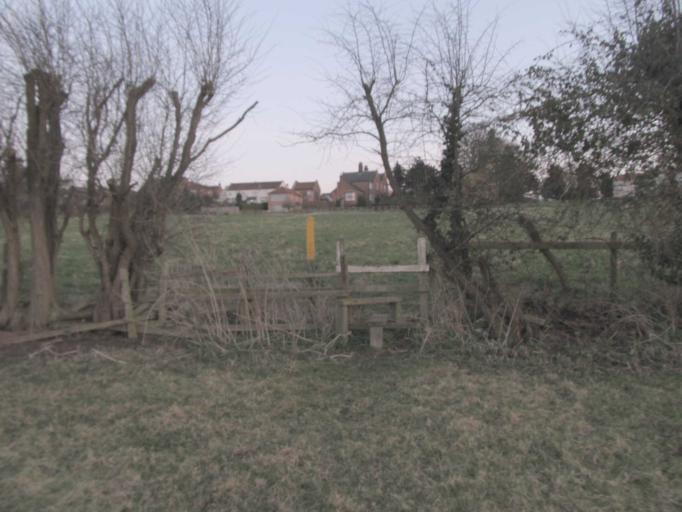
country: GB
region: England
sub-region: Nottinghamshire
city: Misterton
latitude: 53.4095
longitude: -0.8896
